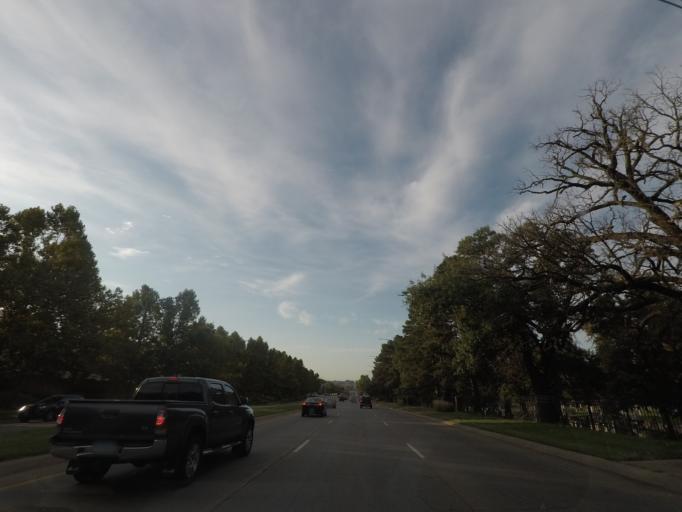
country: US
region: Iowa
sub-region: Polk County
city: Des Moines
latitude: 41.5906
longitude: -93.6449
